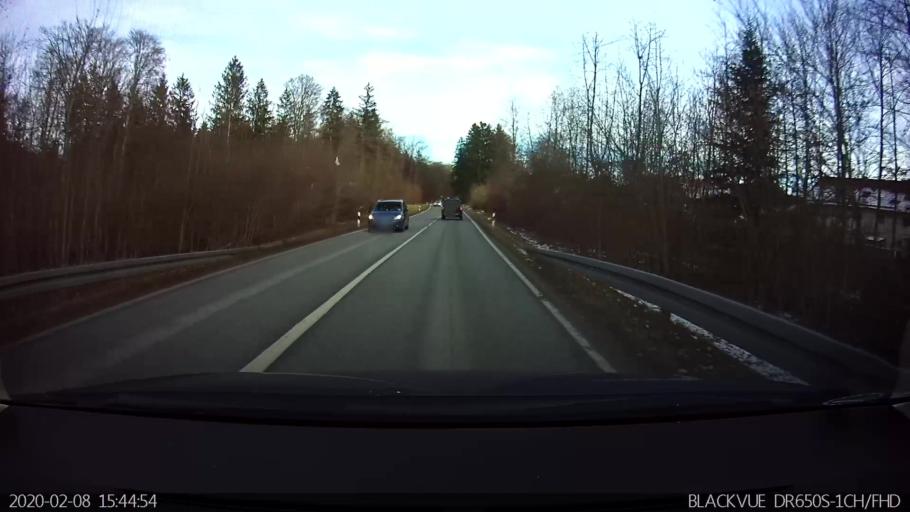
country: DE
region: Bavaria
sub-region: Upper Bavaria
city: Geretsried
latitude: 47.8615
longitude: 11.4762
